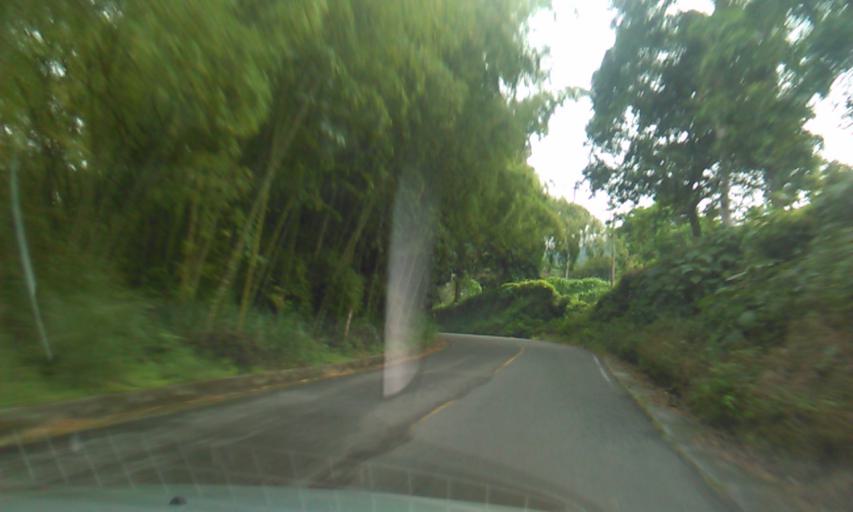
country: CO
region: Quindio
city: Cordoba
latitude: 4.4101
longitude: -75.7033
